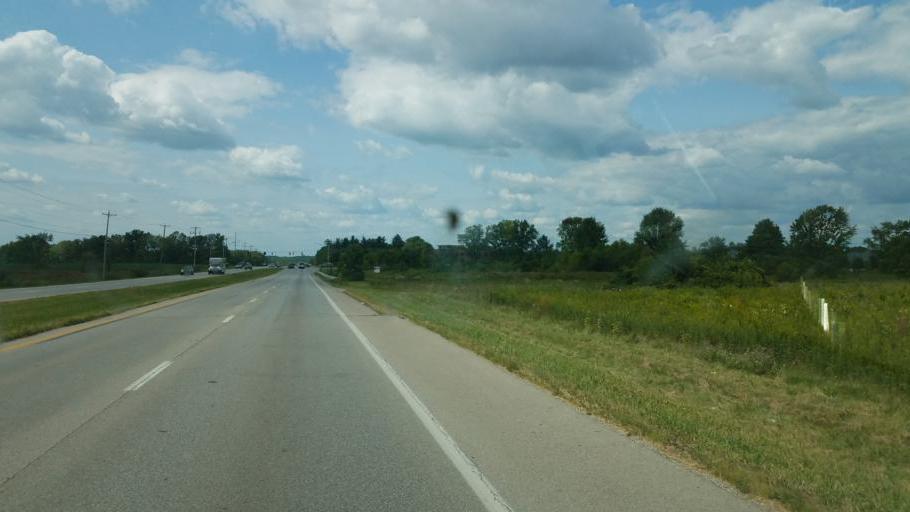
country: US
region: Ohio
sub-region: Delaware County
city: Lewis Center
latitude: 40.2393
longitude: -83.0485
